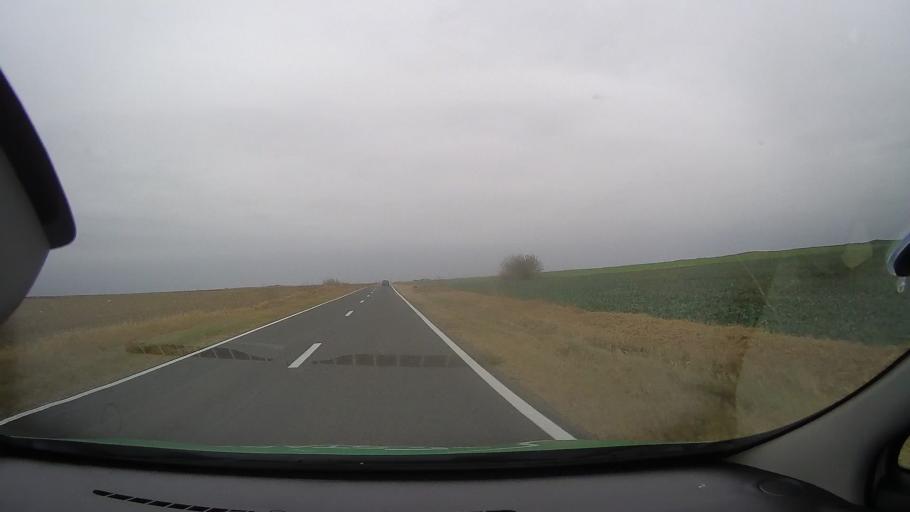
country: RO
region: Constanta
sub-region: Comuna Ciobanu
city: Ciobanu
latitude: 44.7030
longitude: 28.0312
